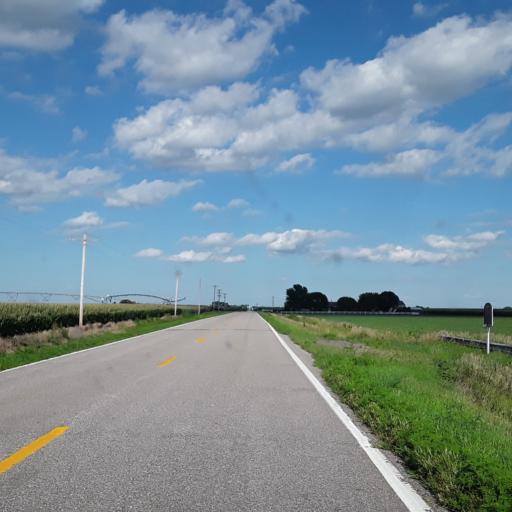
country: US
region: Nebraska
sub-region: Hall County
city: Wood River
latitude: 40.8877
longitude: -98.6250
